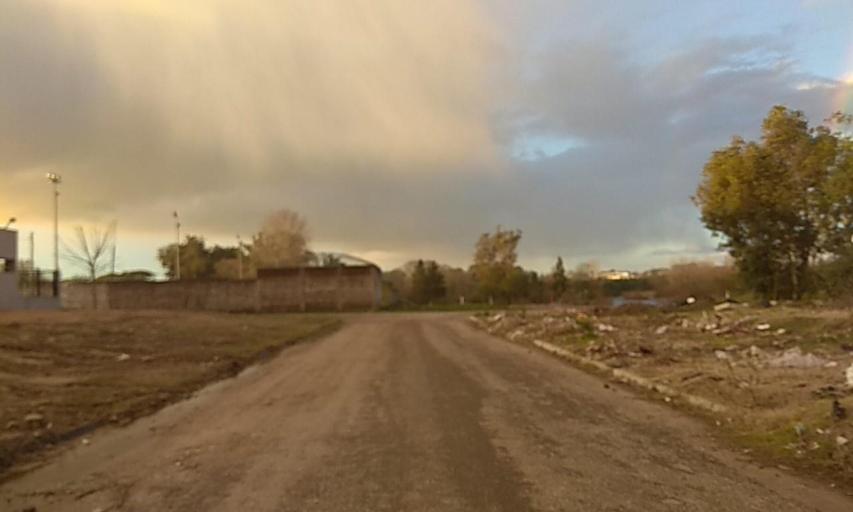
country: UY
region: Florida
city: Florida
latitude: -34.1036
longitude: -56.2049
